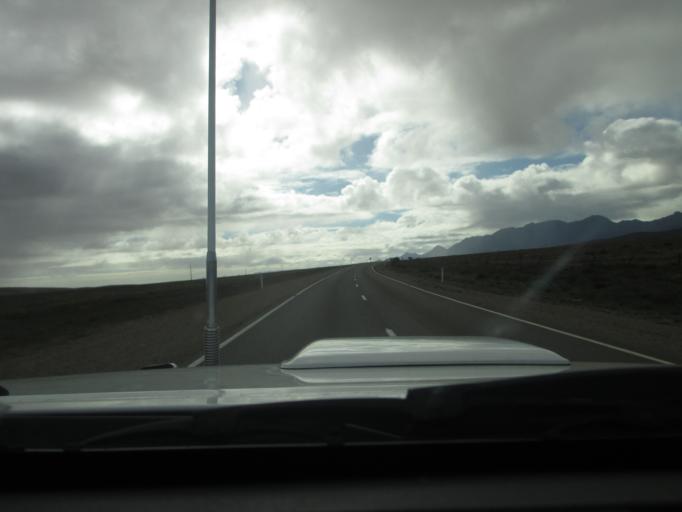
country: AU
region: South Australia
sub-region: Flinders Ranges
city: Quorn
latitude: -31.5997
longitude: 138.4036
